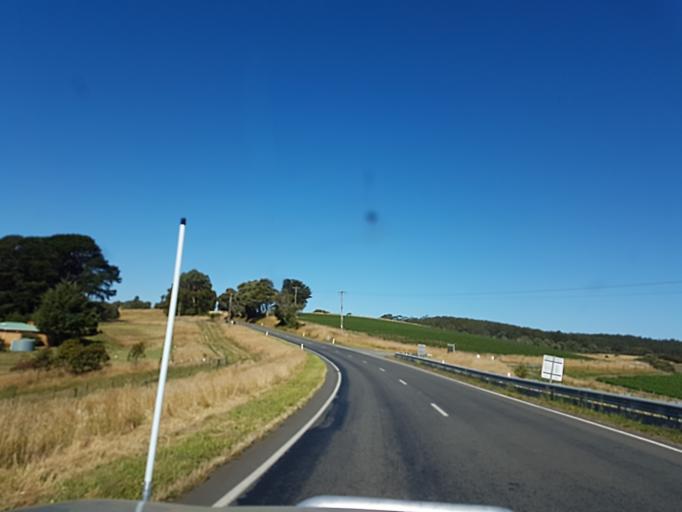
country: AU
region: Victoria
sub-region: Colac-Otway
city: Apollo Bay
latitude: -38.6334
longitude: 143.5107
